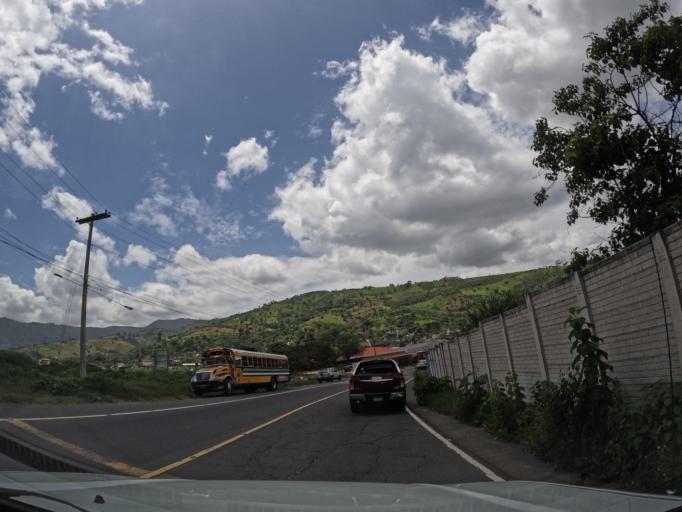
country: GT
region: Sacatepequez
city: San Antonio Aguas Calientes
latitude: 14.5340
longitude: -90.7694
